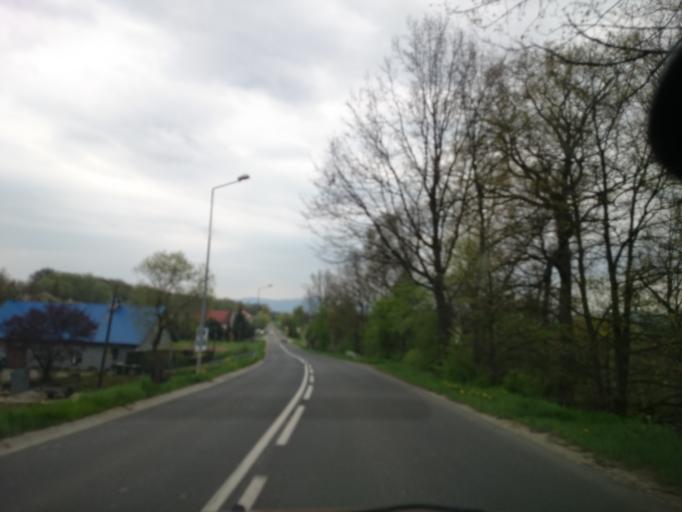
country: PL
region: Opole Voivodeship
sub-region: Powiat nyski
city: Glucholazy
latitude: 50.3753
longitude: 17.3592
